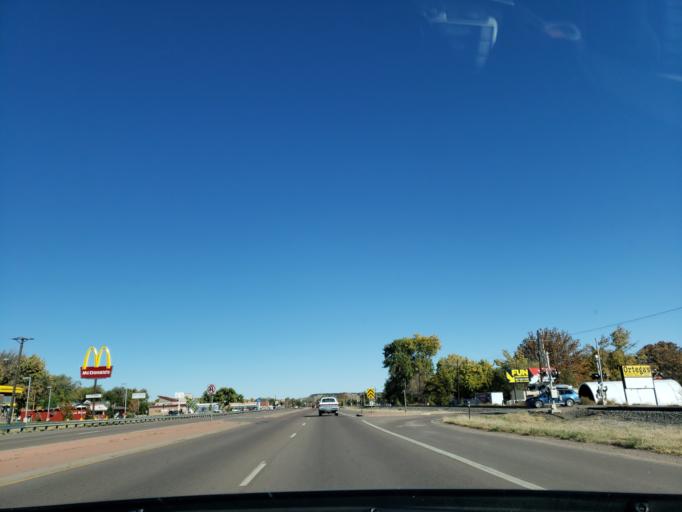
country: US
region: Colorado
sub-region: Fremont County
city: Lincoln Park
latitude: 38.4479
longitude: -105.2147
